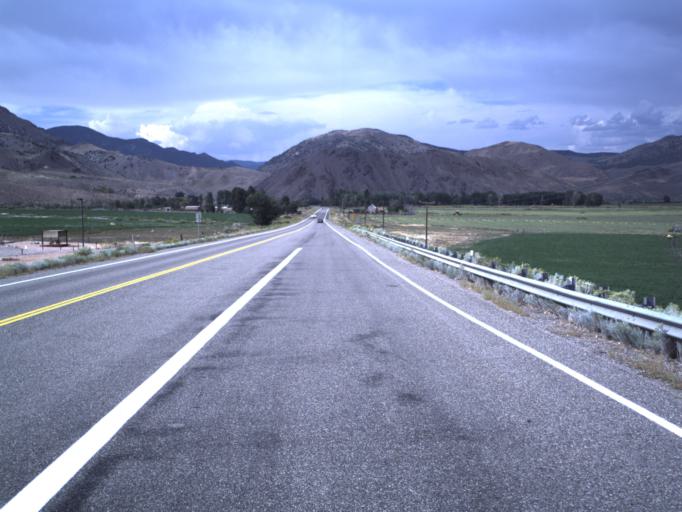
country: US
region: Utah
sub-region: Sevier County
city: Monroe
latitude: 38.4612
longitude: -112.2325
